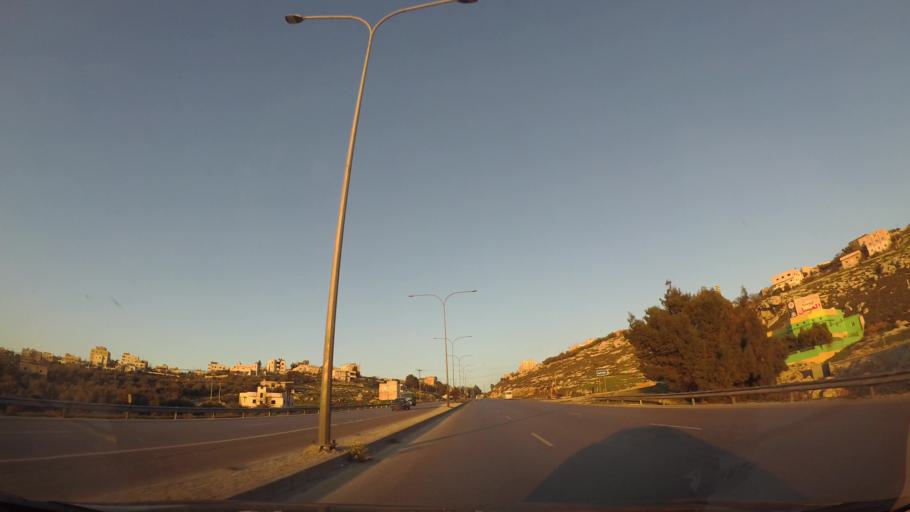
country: JO
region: Amman
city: Umm as Summaq
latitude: 31.8609
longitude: 35.8125
